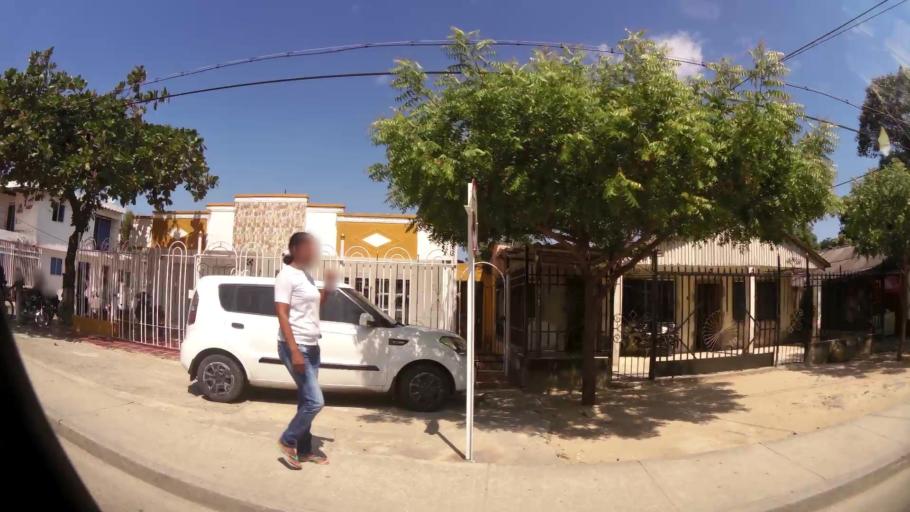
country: CO
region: Atlantico
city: Barranquilla
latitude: 10.9643
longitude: -74.8266
